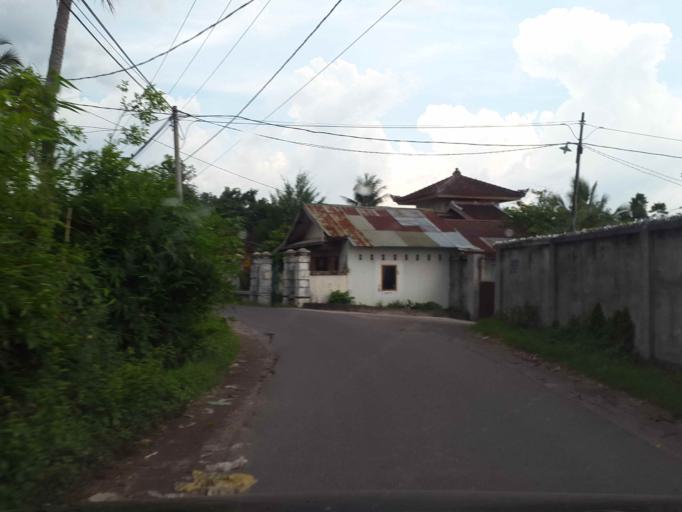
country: ID
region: West Nusa Tenggara
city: Kekeri
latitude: -8.5547
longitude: 116.1122
